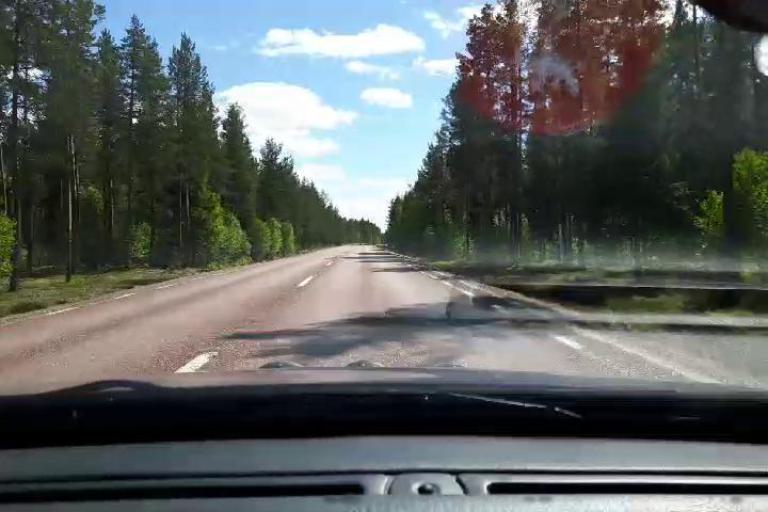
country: SE
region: Gaevleborg
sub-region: Ljusdals Kommun
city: Farila
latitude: 61.8272
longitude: 15.7539
